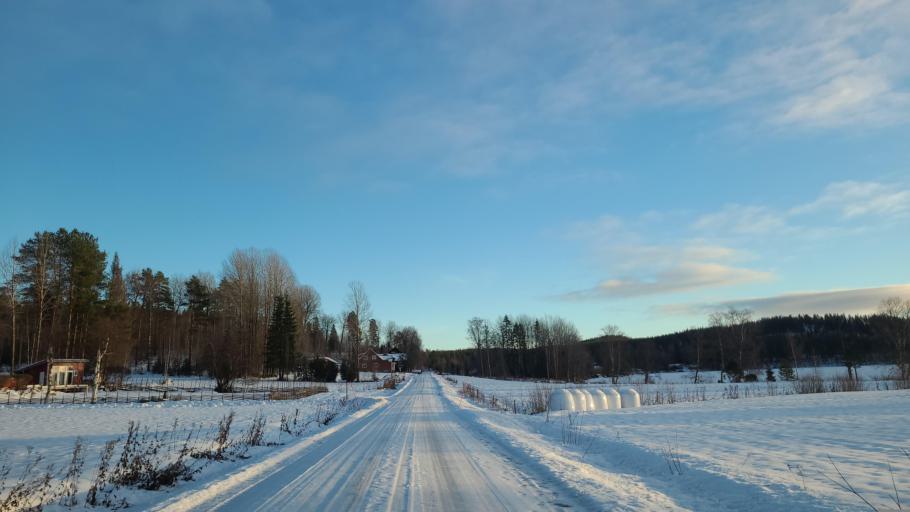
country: SE
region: Gaevleborg
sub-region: Bollnas Kommun
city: Kilafors
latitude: 61.3965
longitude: 16.6766
